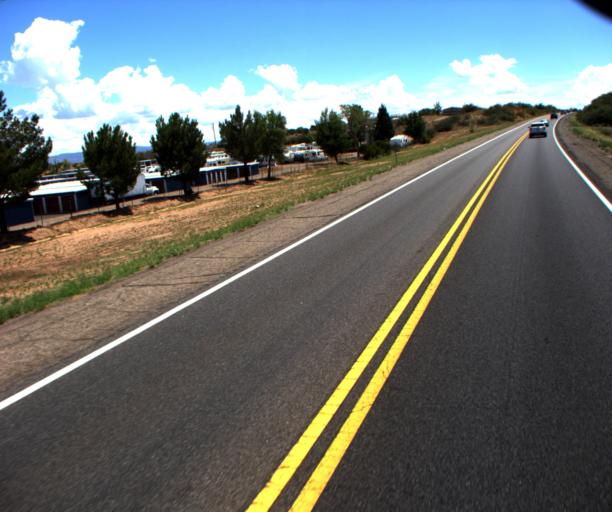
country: US
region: Arizona
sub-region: Yavapai County
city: Camp Verde
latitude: 34.6177
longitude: -111.9183
